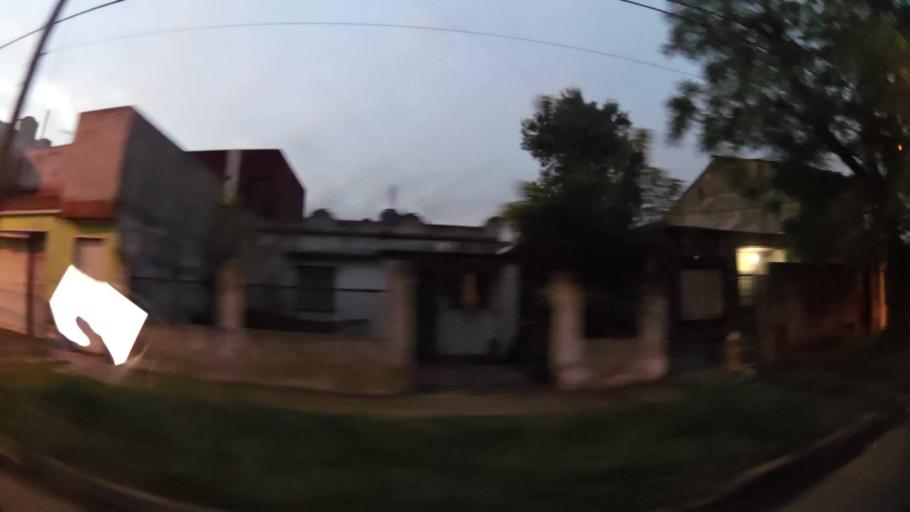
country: AR
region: Buenos Aires
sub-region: Partido de Lomas de Zamora
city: Lomas de Zamora
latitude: -34.7470
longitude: -58.3613
